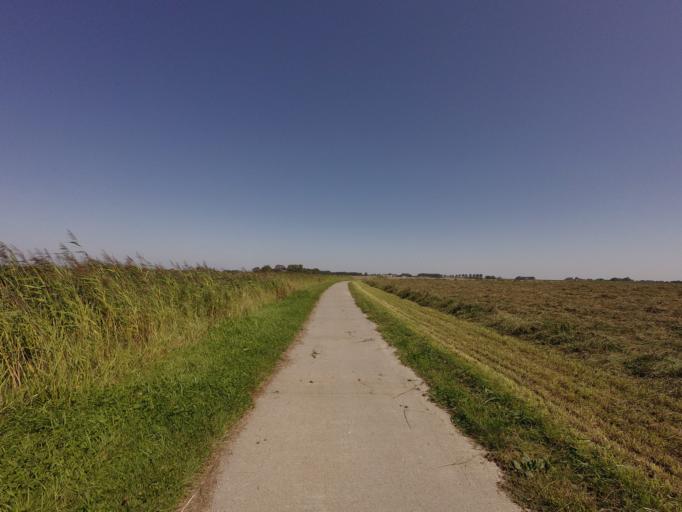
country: NL
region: Friesland
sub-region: Gemeente Dongeradeel
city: Anjum
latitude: 53.3934
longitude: 6.0691
